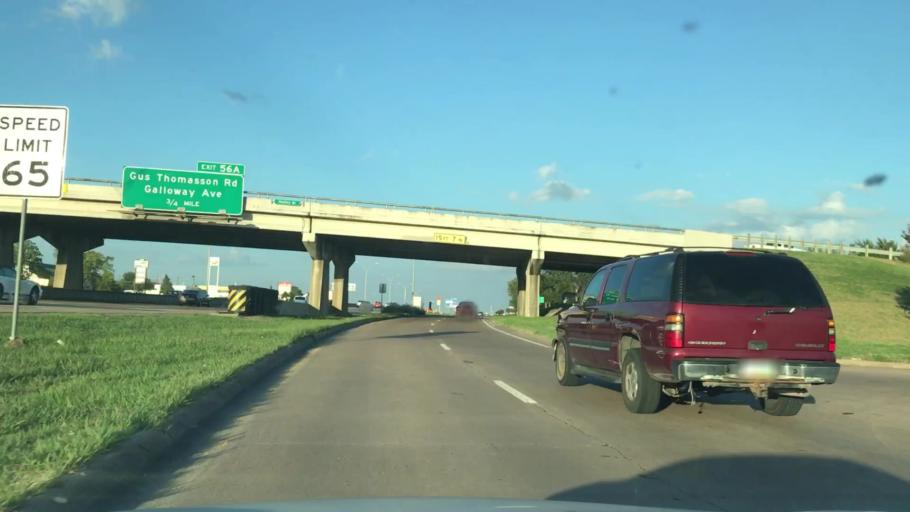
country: US
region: Texas
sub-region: Dallas County
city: Mesquite
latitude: 32.8095
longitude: -96.6553
